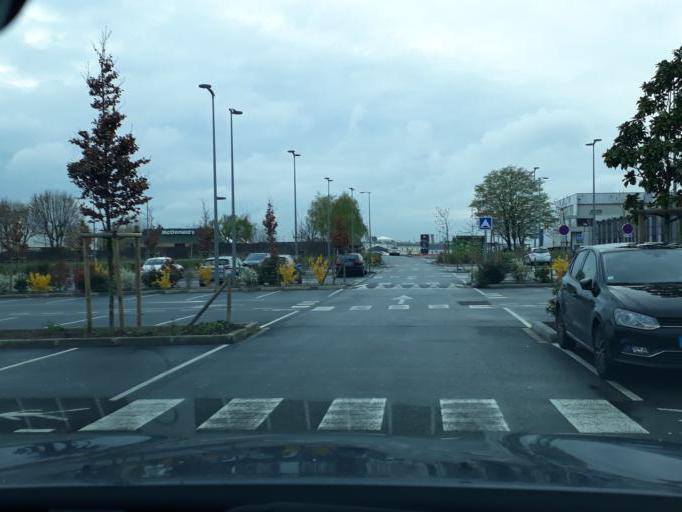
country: FR
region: Centre
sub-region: Departement du Loiret
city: Saint-Jean-de-la-Ruelle
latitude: 47.9065
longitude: 1.8672
